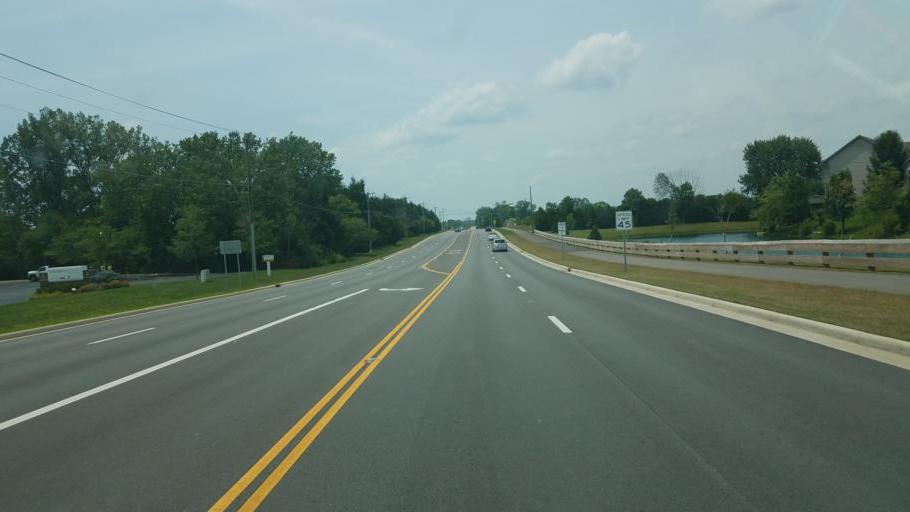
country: US
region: Ohio
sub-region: Delaware County
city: Powell
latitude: 40.1588
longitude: -83.0997
